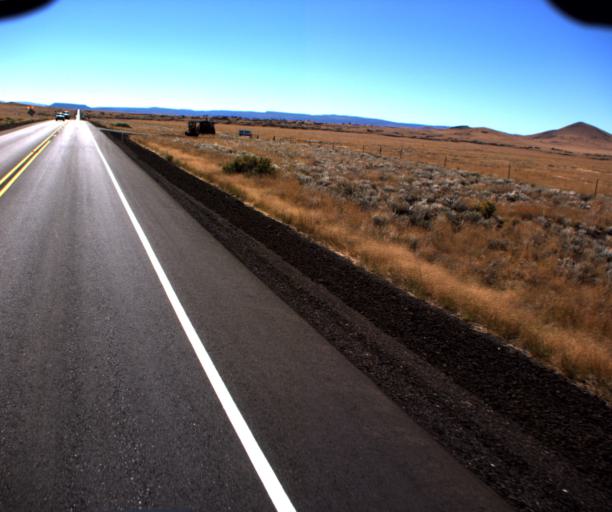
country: US
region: Arizona
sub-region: Apache County
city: Springerville
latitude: 34.2705
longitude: -109.3615
